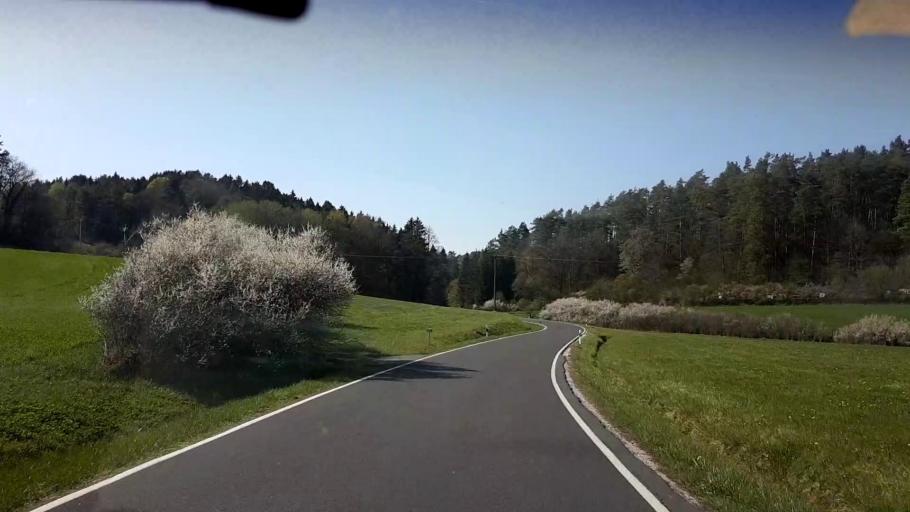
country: DE
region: Bavaria
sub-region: Upper Franconia
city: Waischenfeld
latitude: 49.8078
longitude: 11.3680
